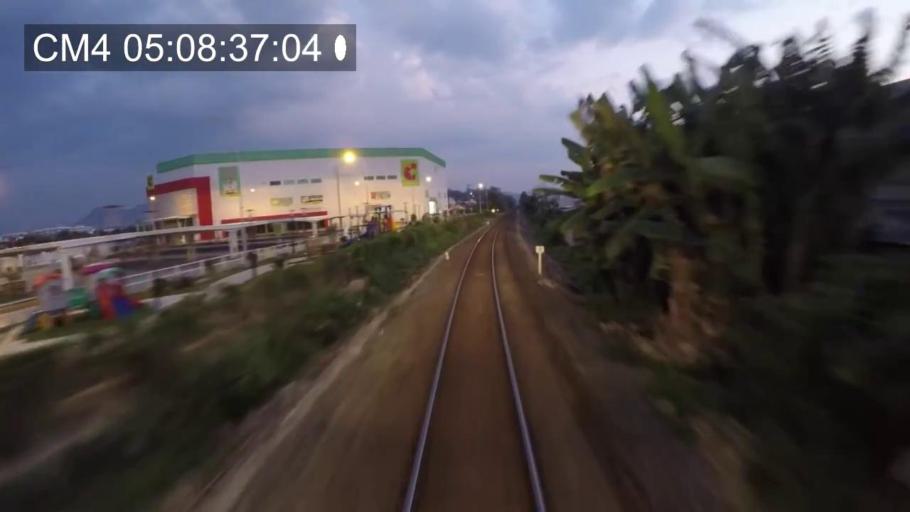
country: VN
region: Khanh Hoa
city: Nha Trang
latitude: 12.2940
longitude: 109.1865
